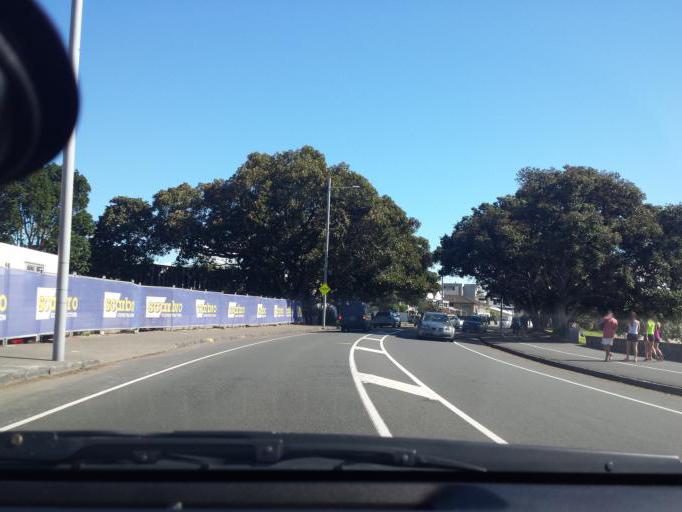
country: NZ
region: Auckland
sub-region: Auckland
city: Tamaki
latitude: -36.8509
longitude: 174.8478
